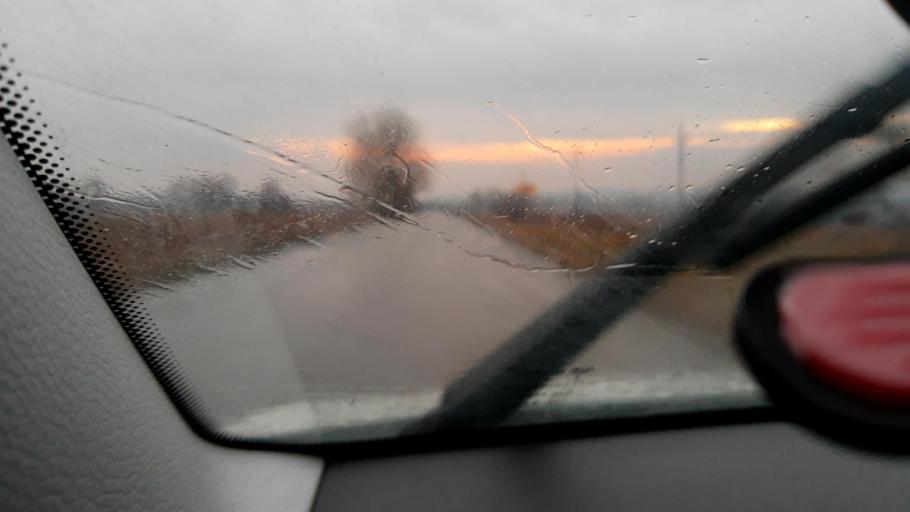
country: RU
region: Bashkortostan
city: Blagoveshchensk
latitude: 54.8921
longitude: 56.1483
